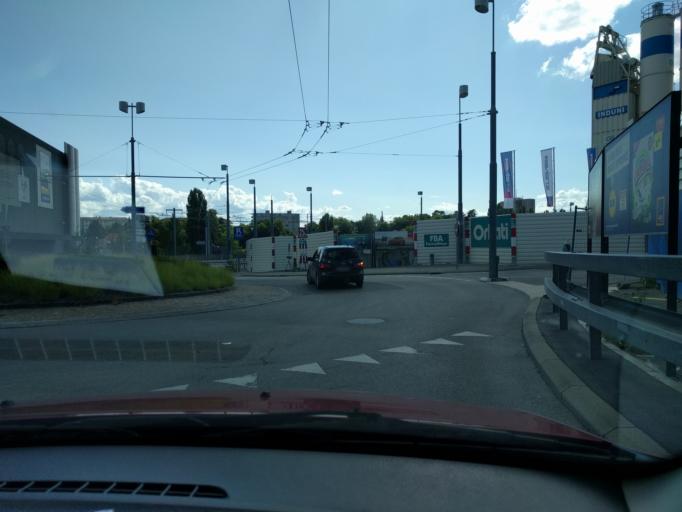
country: CH
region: Vaud
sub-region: Ouest Lausannois District
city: Prilly
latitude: 46.5282
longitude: 6.6015
